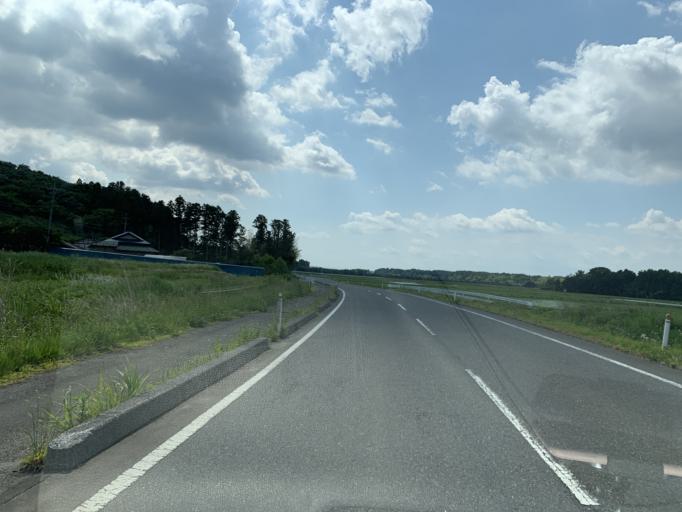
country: JP
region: Miyagi
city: Furukawa
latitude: 38.6820
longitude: 140.9757
